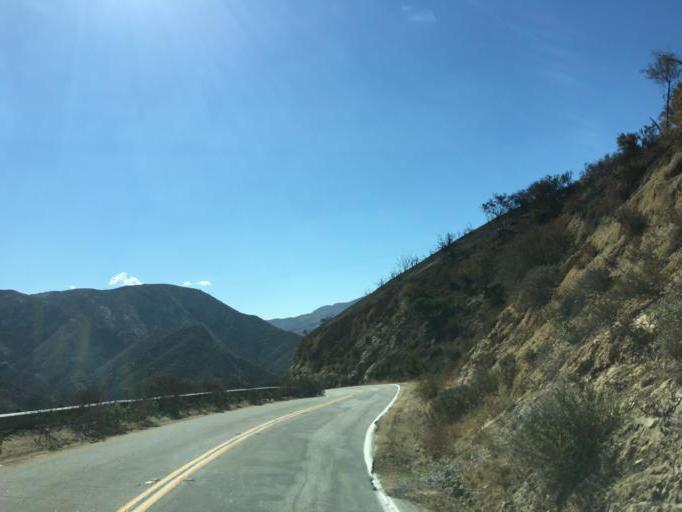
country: US
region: California
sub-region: Los Angeles County
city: San Fernando
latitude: 34.3384
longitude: -118.3414
